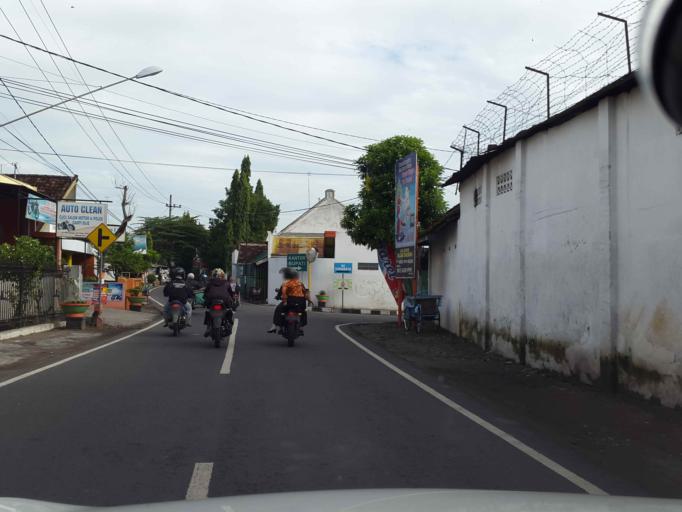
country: ID
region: East Java
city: Mojokerto
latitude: -7.4663
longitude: 112.4296
